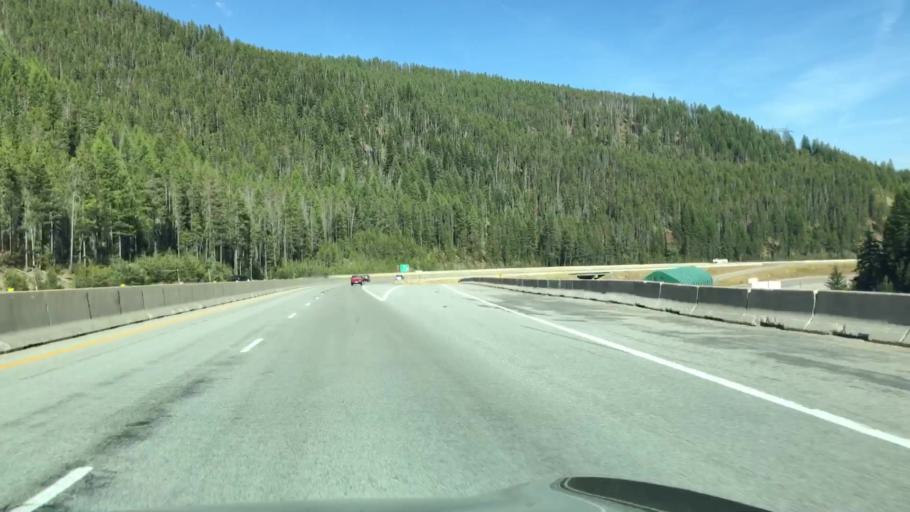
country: US
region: Montana
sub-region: Sanders County
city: Thompson Falls
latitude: 47.4211
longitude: -115.6118
